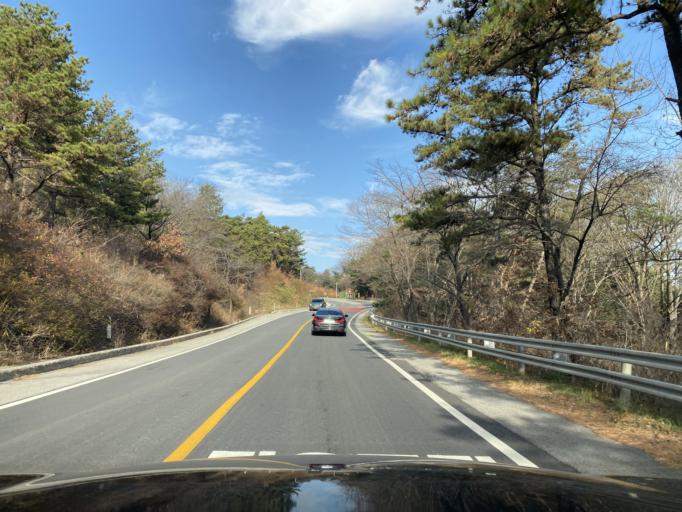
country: KR
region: Chungcheongnam-do
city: Hongsung
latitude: 36.6632
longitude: 126.6334
